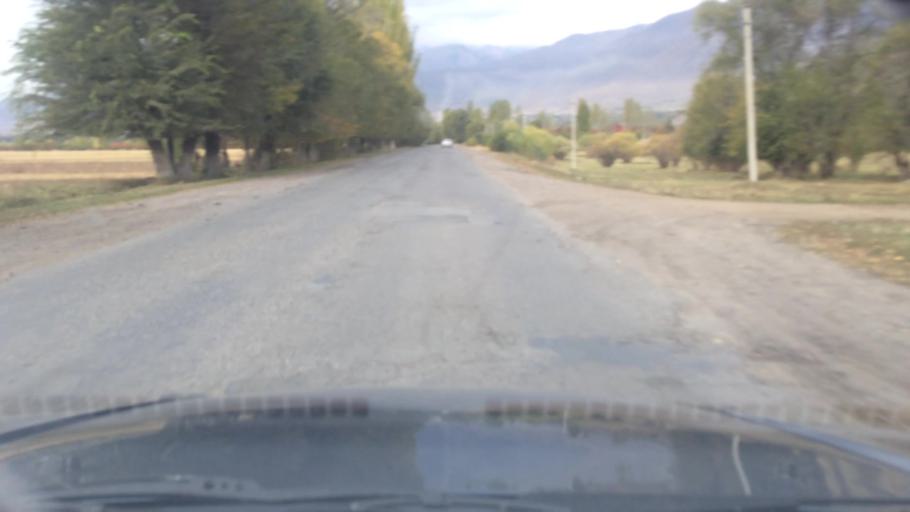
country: KG
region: Ysyk-Koel
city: Tyup
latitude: 42.7834
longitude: 78.2791
